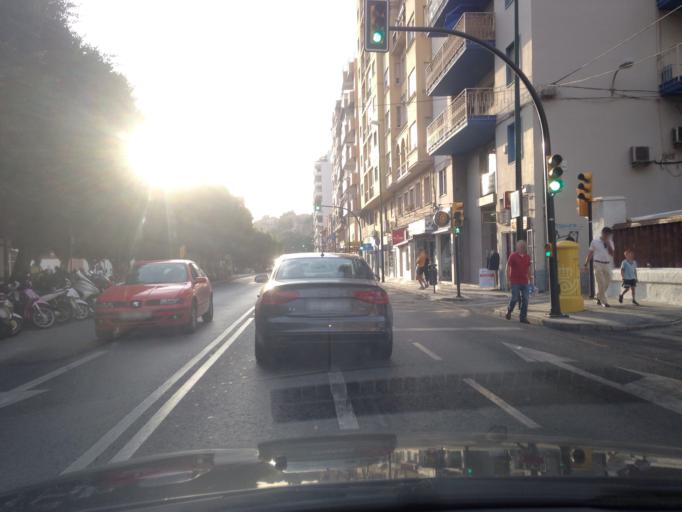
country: ES
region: Andalusia
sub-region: Provincia de Malaga
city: Malaga
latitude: 36.7209
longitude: -4.4094
